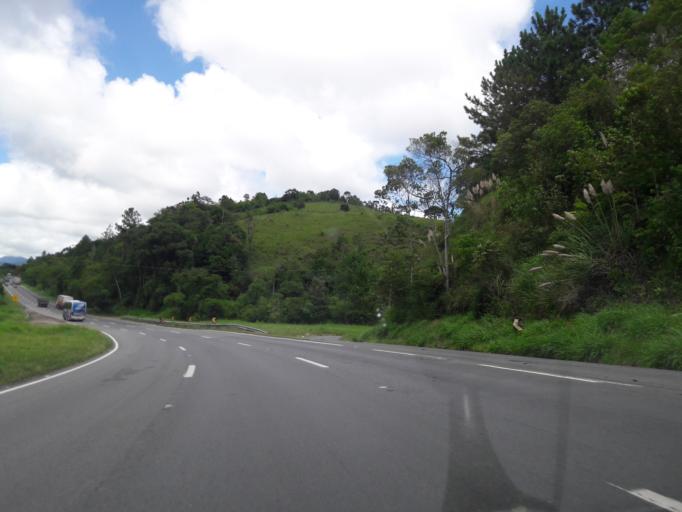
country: BR
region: Sao Paulo
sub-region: Cajati
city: Cajati
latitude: -24.9751
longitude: -48.5052
